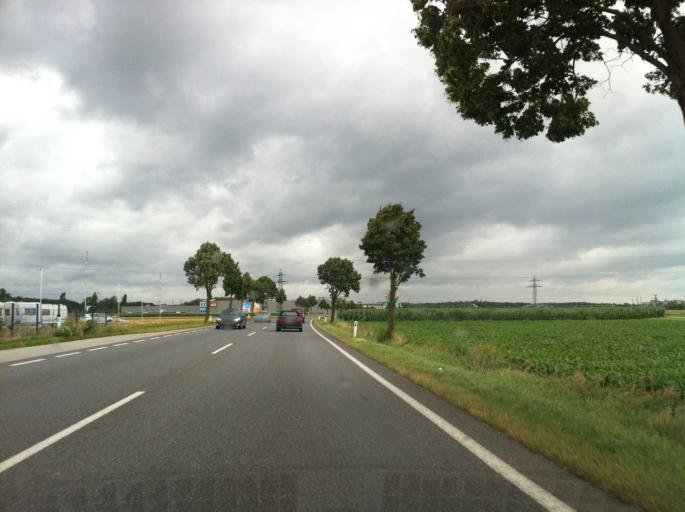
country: AT
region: Lower Austria
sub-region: Politischer Bezirk Tulln
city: Langenrohr
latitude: 48.3119
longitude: 16.0151
